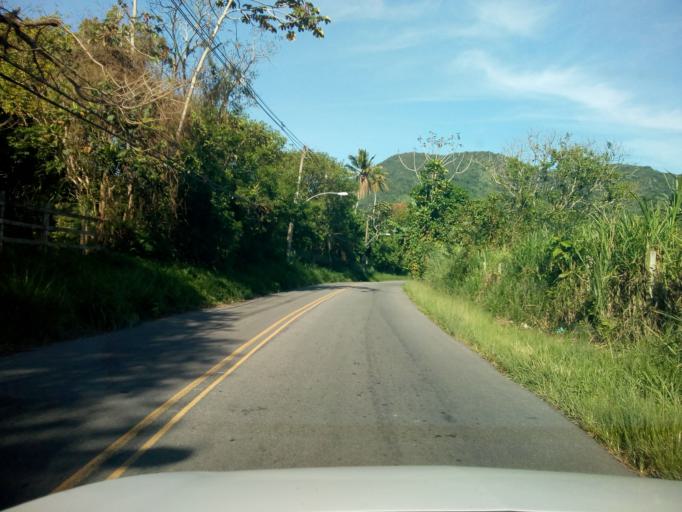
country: BR
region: Rio de Janeiro
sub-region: Nilopolis
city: Nilopolis
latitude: -23.0257
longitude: -43.5109
